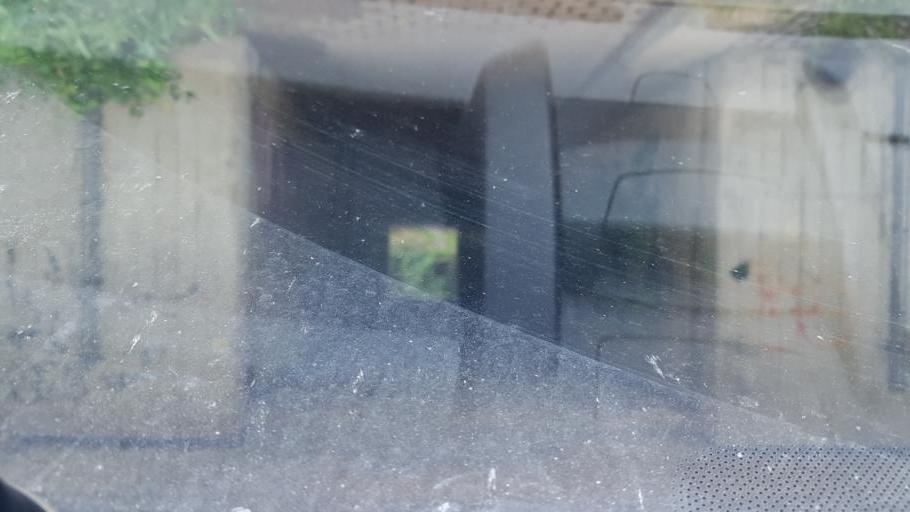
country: DE
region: Saxony
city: Grossrohrsdorf
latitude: 51.1607
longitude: 14.0381
